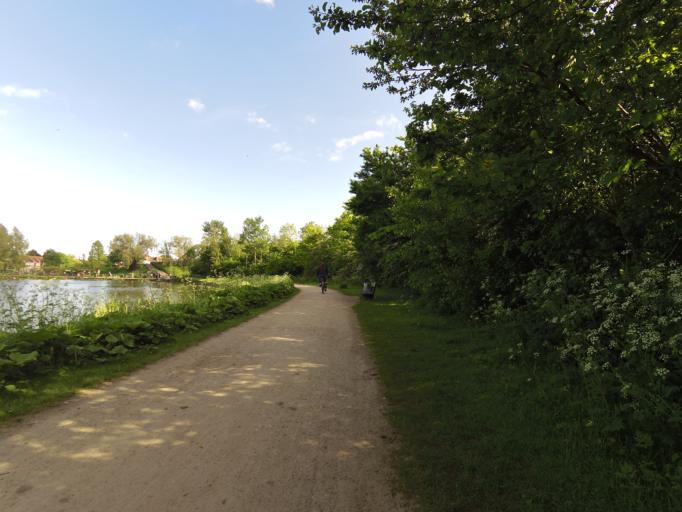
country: DK
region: Capital Region
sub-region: Lyngby-Tarbaek Kommune
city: Kongens Lyngby
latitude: 55.7443
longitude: 12.5339
